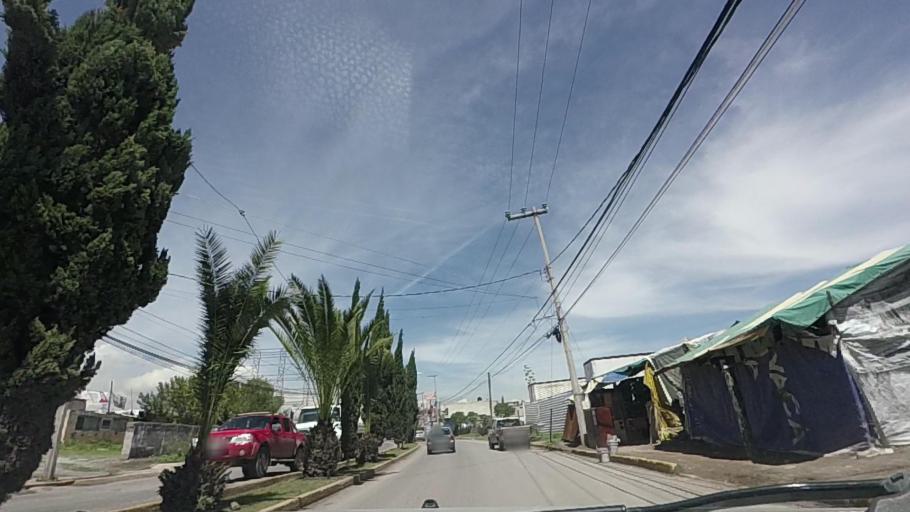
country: MX
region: Mexico
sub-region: Huehuetoca
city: Casa Nueva
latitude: 19.8309
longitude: -99.2250
